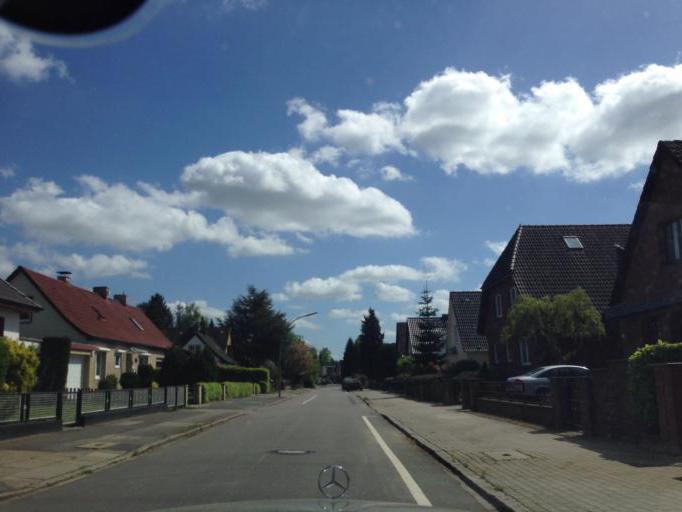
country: DE
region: Schleswig-Holstein
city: Barsbuettel
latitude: 53.5929
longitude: 10.1521
